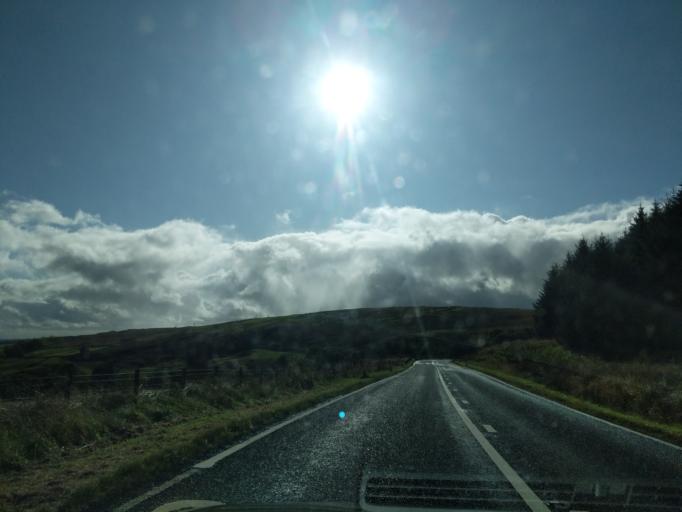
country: GB
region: Scotland
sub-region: Dumfries and Galloway
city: Moffat
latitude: 55.3654
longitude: -3.4752
